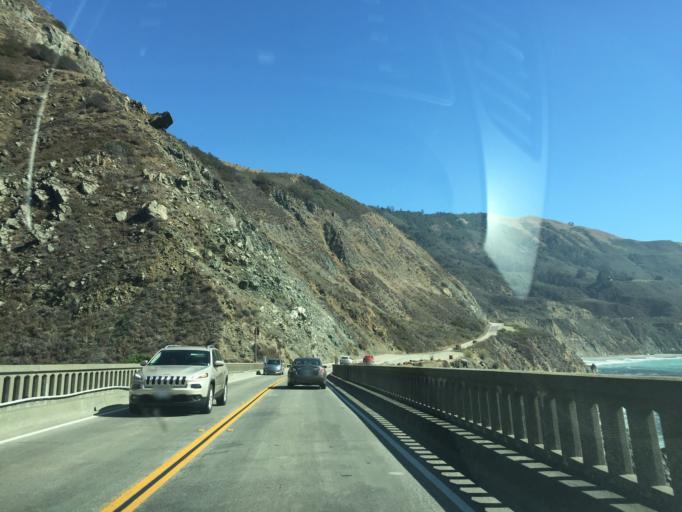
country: US
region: California
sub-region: Monterey County
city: Greenfield
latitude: 36.0700
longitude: -121.5999
